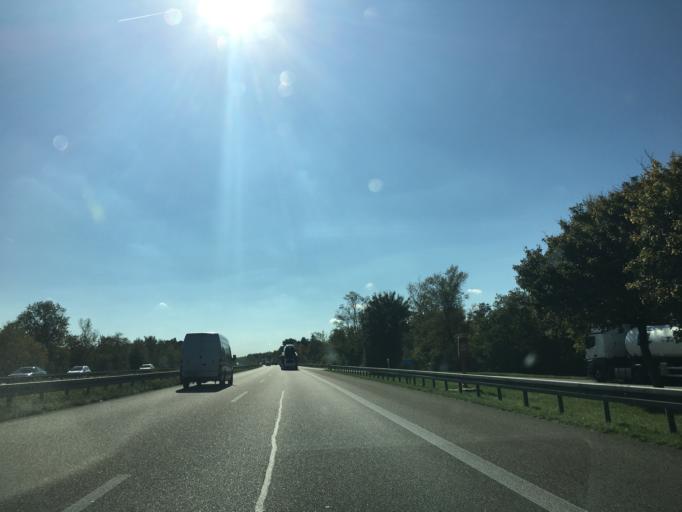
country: FR
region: Alsace
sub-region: Departement du Haut-Rhin
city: Blodelsheim
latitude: 47.8733
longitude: 7.5691
